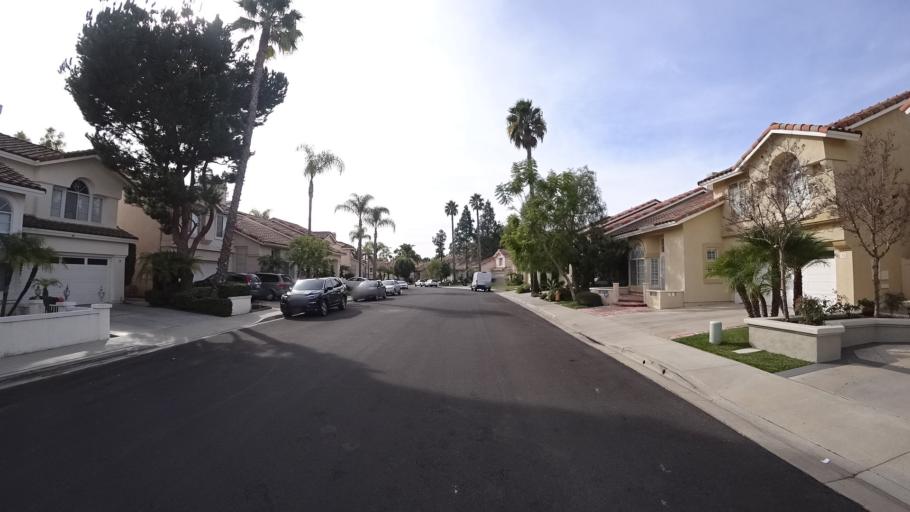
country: US
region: California
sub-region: Orange County
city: Laguna Woods
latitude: 33.6048
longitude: -117.7370
